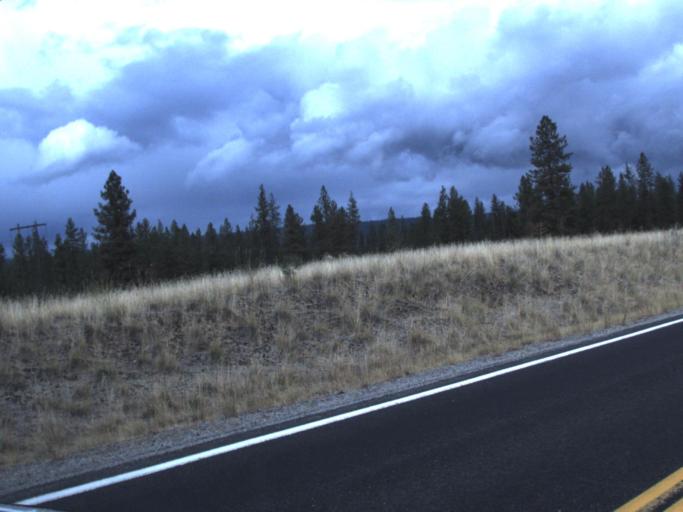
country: US
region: Washington
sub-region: Spokane County
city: Fairchild Air Force Base
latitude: 47.8839
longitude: -117.8386
